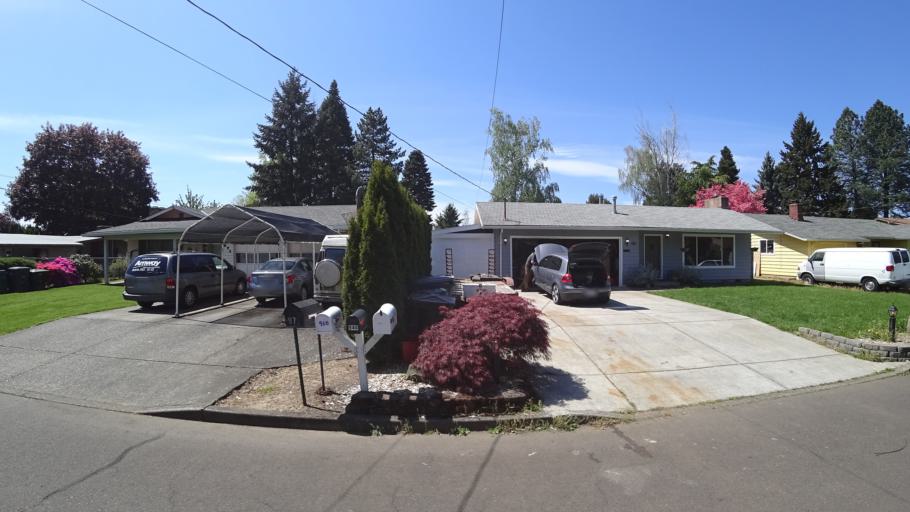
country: US
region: Oregon
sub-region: Washington County
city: Hillsboro
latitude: 45.5122
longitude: -122.9665
